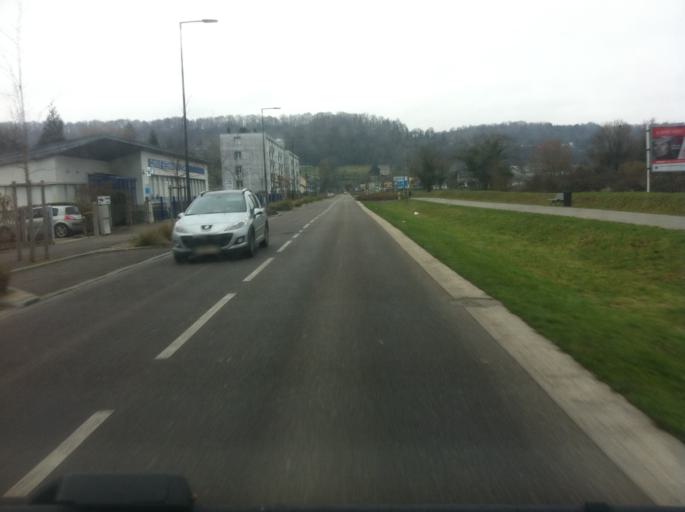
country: FR
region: Haute-Normandie
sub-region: Departement de l'Eure
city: Saint-Germain-Village
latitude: 49.3564
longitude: 0.5010
